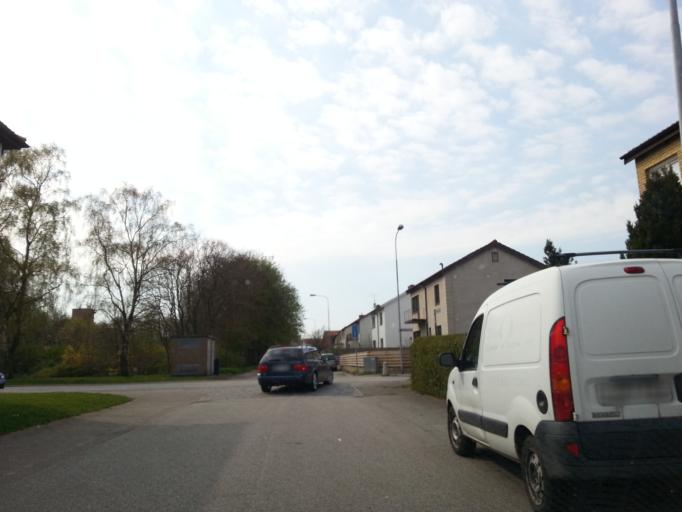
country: SE
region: Skane
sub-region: Trelleborgs Kommun
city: Trelleborg
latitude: 55.3725
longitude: 13.1792
